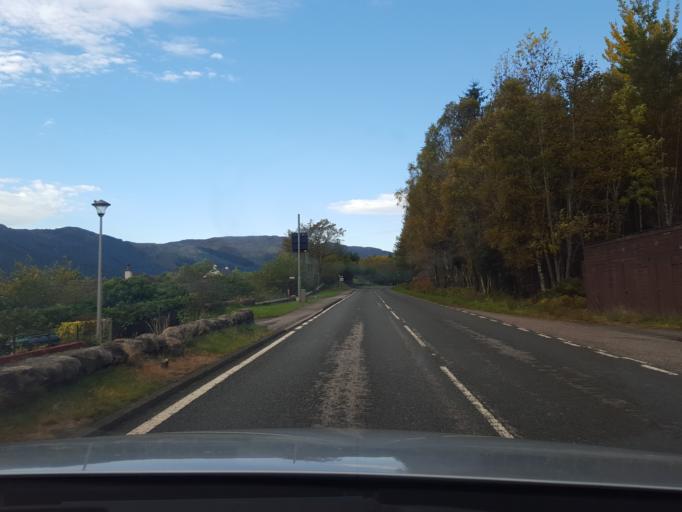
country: GB
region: Scotland
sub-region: Highland
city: Fort William
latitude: 57.2337
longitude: -5.4229
